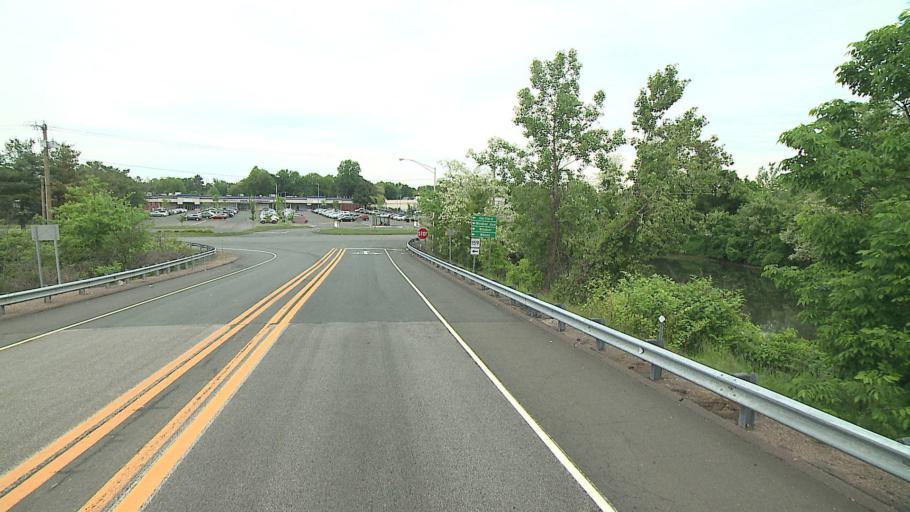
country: US
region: Connecticut
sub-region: Hartford County
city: South Windsor
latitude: 41.8054
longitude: -72.6573
